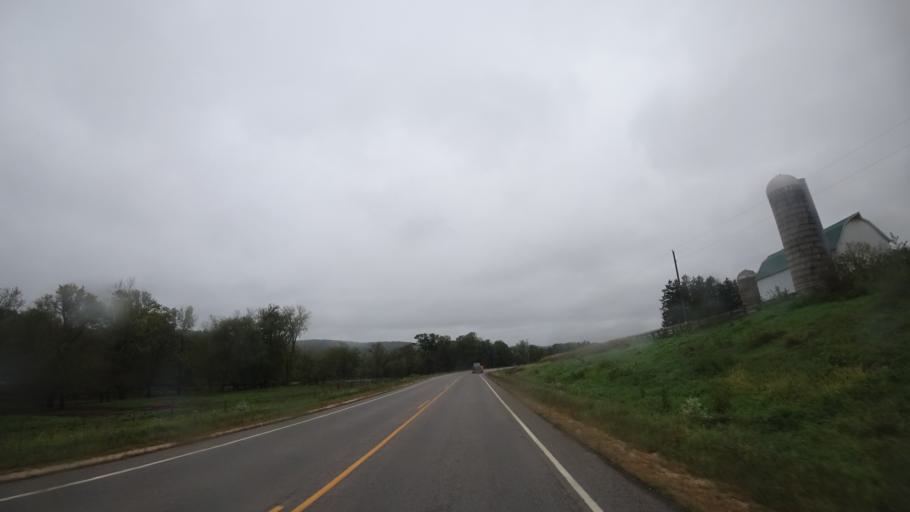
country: US
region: Wisconsin
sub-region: Crawford County
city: Prairie du Chien
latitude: 43.0356
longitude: -90.9887
